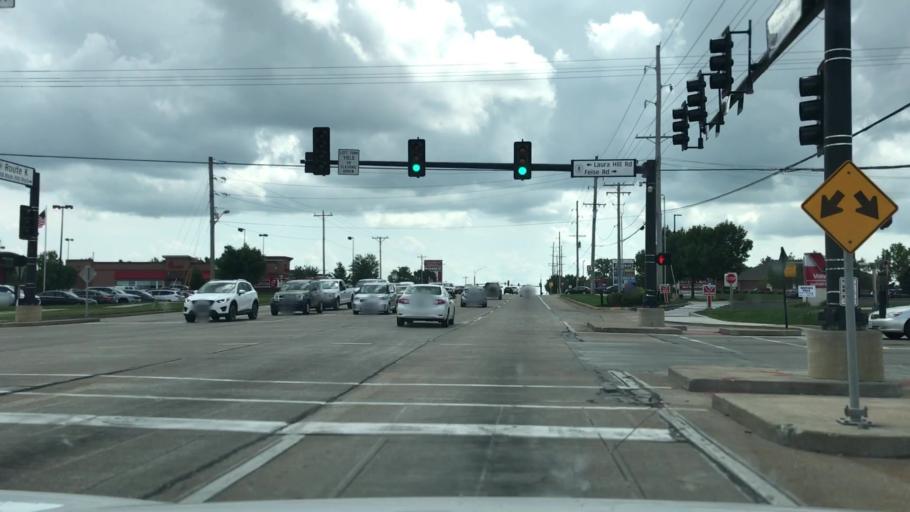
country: US
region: Missouri
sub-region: Saint Charles County
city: O'Fallon
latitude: 38.7803
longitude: -90.7000
